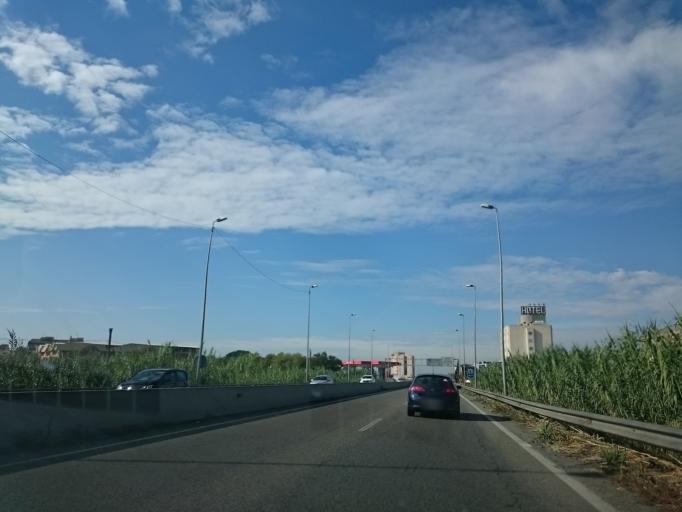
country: ES
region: Catalonia
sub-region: Provincia de Lleida
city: Lleida
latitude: 41.6101
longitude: 0.6393
